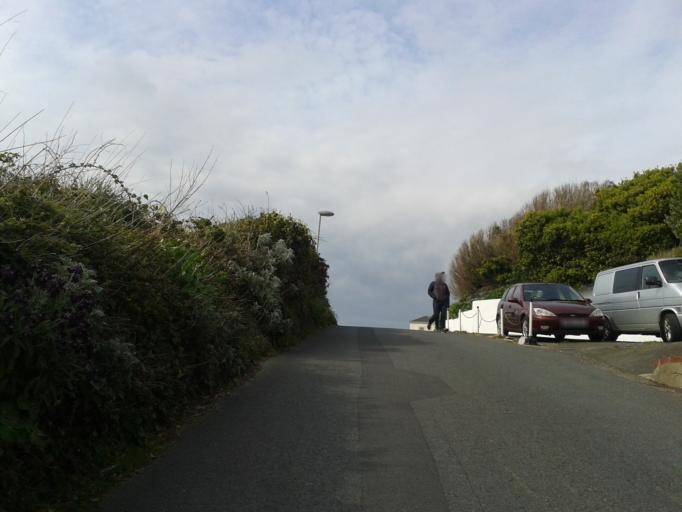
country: GB
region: England
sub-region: Devon
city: Braunton
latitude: 51.1795
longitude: -4.2119
